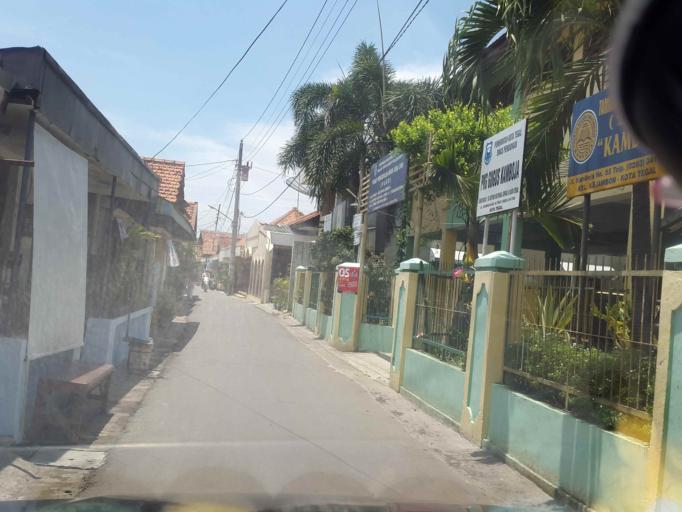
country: ID
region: Central Java
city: Tegal
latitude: -6.8854
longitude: 109.1369
